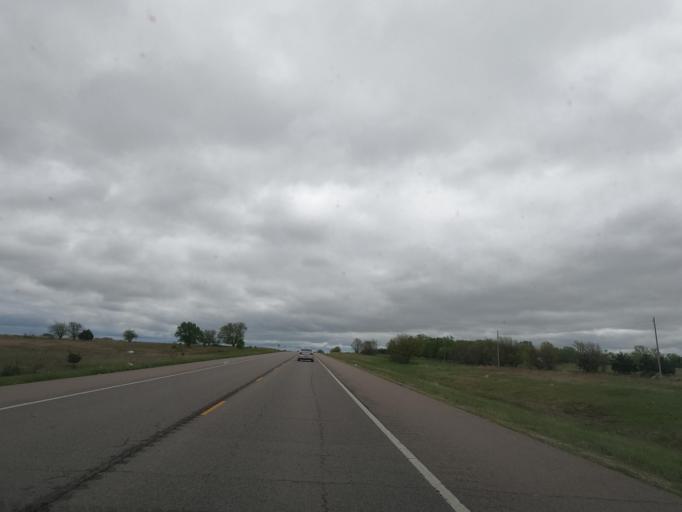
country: US
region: Kansas
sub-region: Elk County
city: Howard
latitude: 37.6360
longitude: -96.2979
